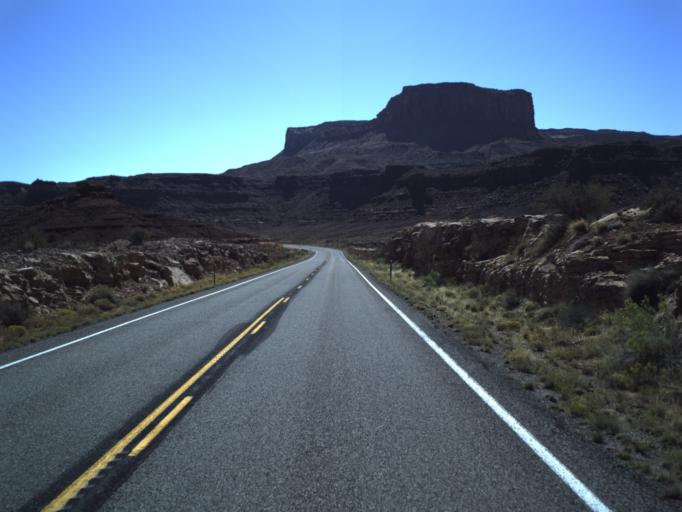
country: US
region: Utah
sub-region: San Juan County
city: Blanding
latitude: 37.8153
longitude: -110.3443
